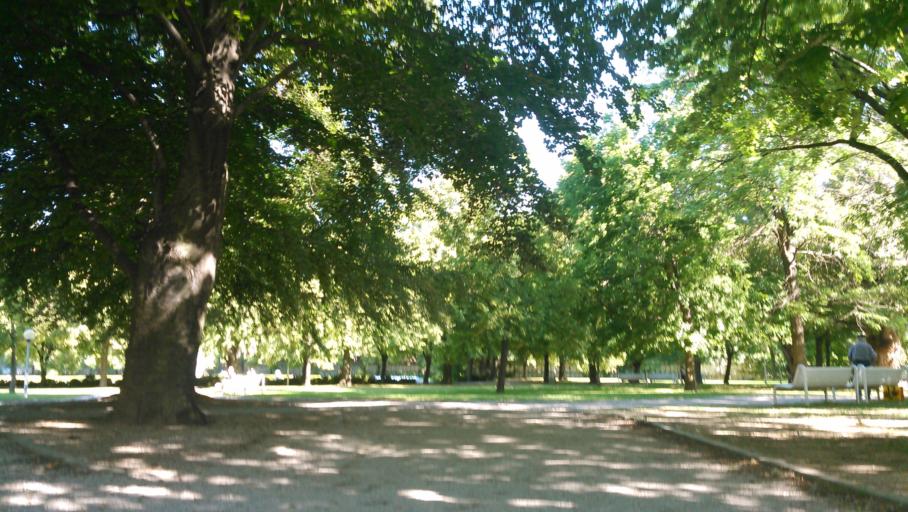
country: SK
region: Bratislavsky
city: Bratislava
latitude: 48.1493
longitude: 17.1201
